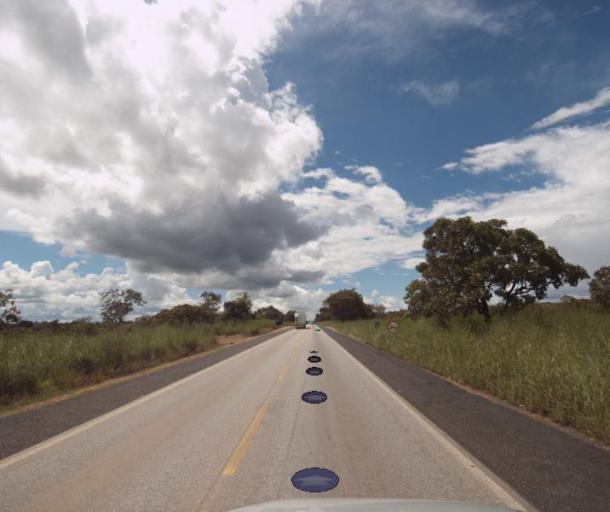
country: BR
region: Goias
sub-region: Uruacu
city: Uruacu
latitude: -14.0198
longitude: -49.0868
